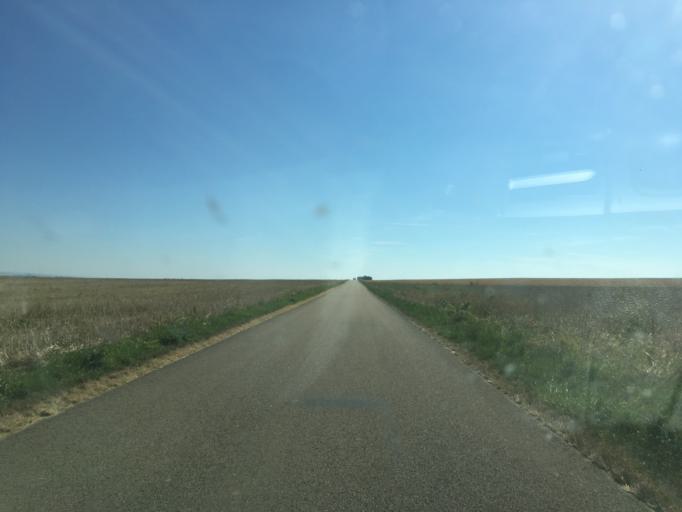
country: FR
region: Bourgogne
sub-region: Departement de l'Yonne
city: Aillant-sur-Tholon
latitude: 47.9157
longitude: 3.3768
